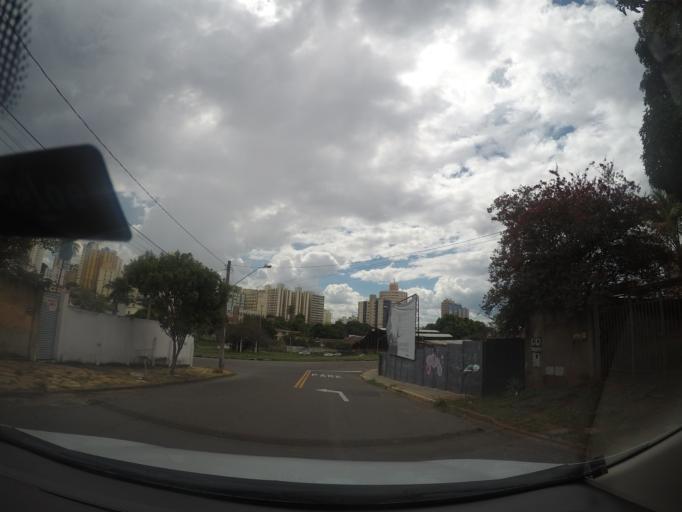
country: BR
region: Goias
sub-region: Goiania
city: Goiania
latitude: -16.6761
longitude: -49.2487
